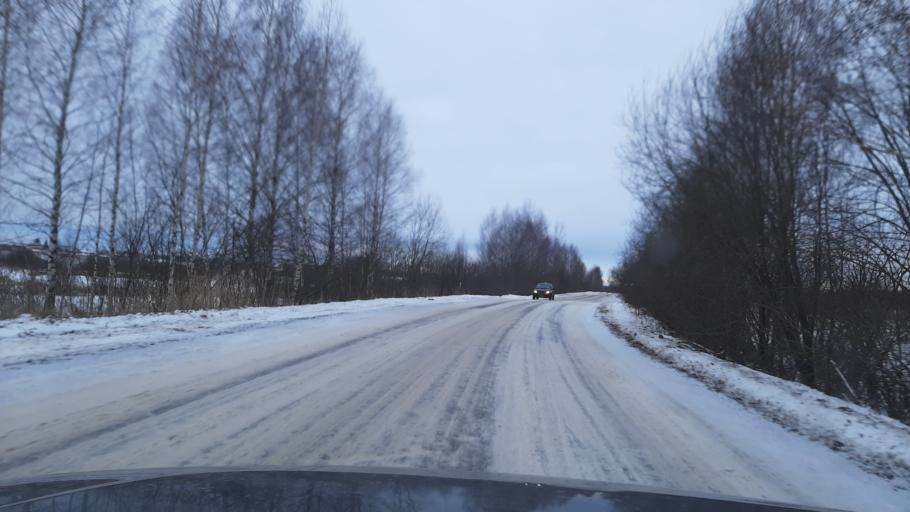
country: RU
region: Kostroma
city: Volgorechensk
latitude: 57.4398
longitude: 41.1083
